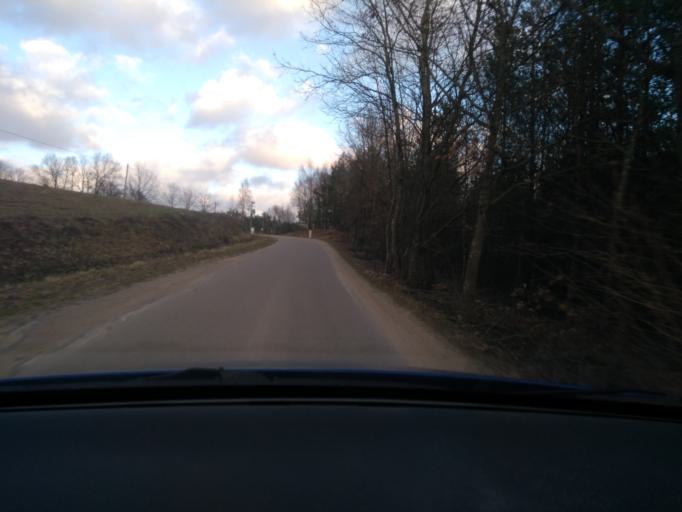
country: PL
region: Pomeranian Voivodeship
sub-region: Powiat kartuski
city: Przodkowo
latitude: 54.4134
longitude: 18.2528
